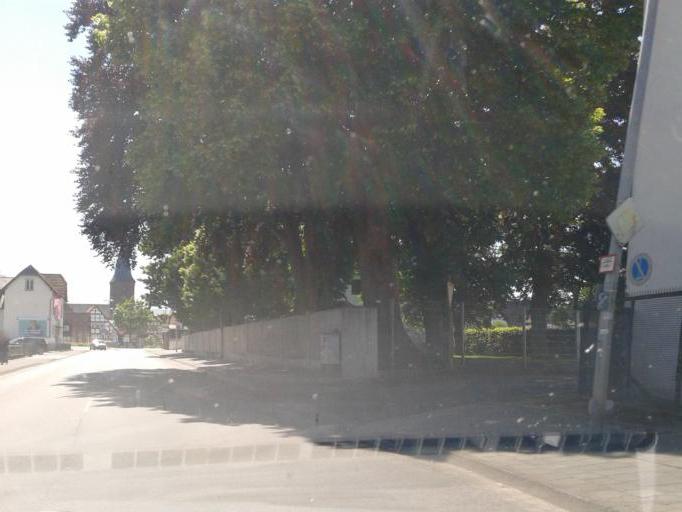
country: DE
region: North Rhine-Westphalia
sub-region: Regierungsbezirk Detmold
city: Lugde
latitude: 51.9613
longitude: 9.2478
